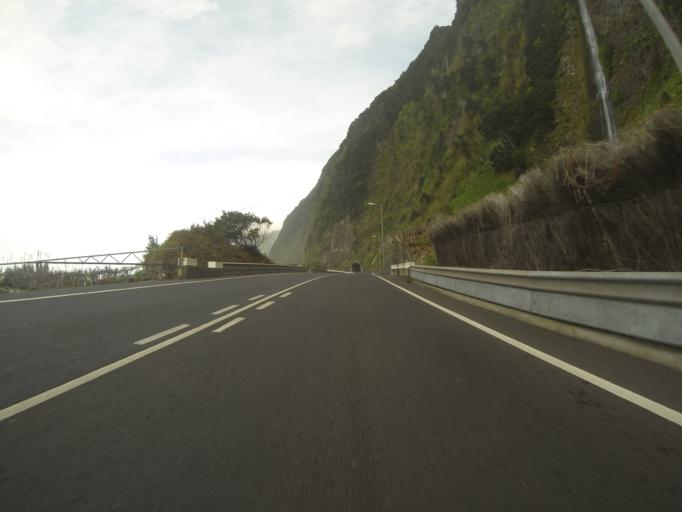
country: PT
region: Madeira
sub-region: Sao Vicente
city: Sao Vicente
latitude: 32.8149
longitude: -17.0793
